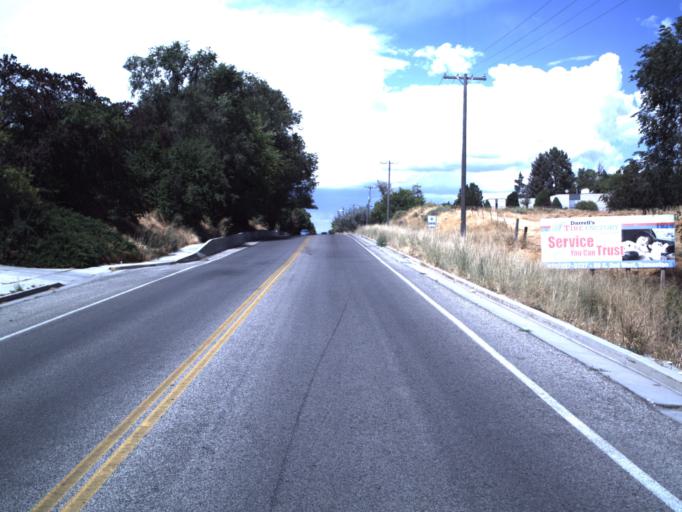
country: US
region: Utah
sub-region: Box Elder County
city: Tremonton
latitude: 41.7144
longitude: -112.1618
